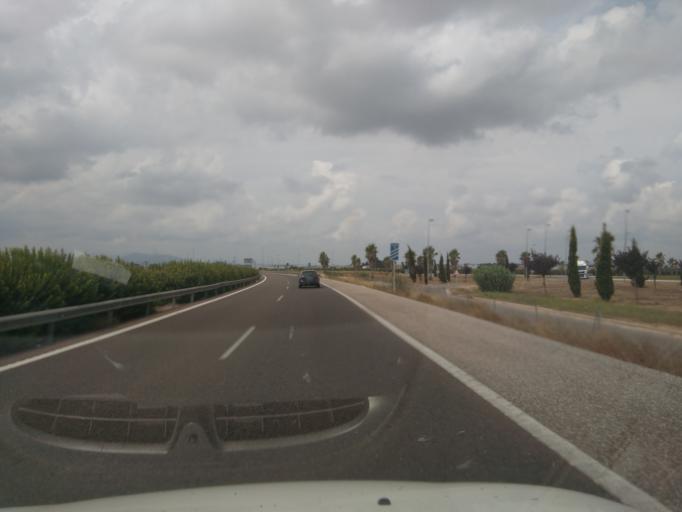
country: ES
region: Valencia
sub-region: Provincia de Valencia
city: Guadassuar
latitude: 39.1741
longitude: -0.4676
